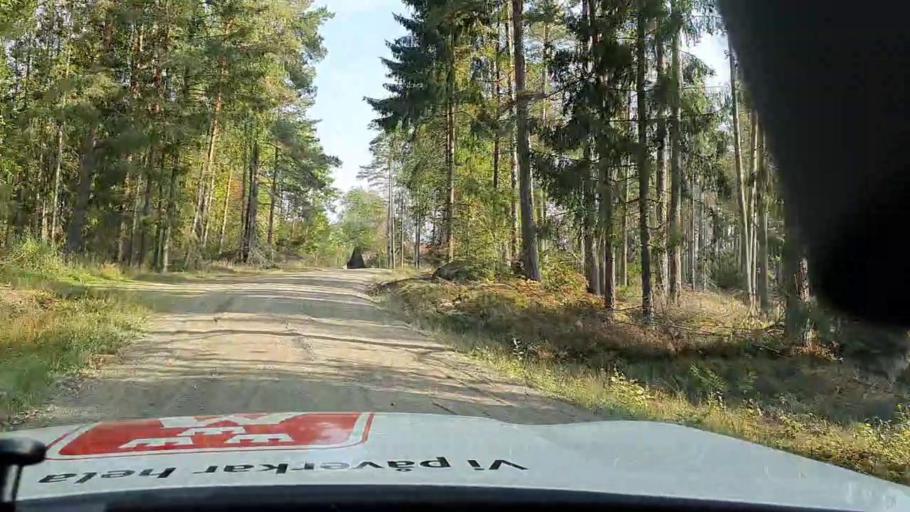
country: SE
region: Vaestmanland
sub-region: Kungsors Kommun
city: Kungsoer
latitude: 59.3477
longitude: 16.1730
